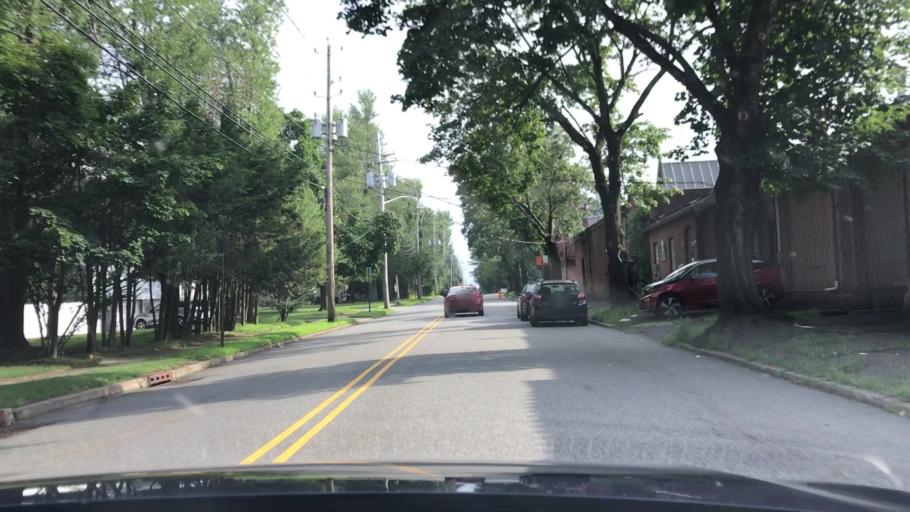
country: US
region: New Jersey
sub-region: Bergen County
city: Closter
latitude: 40.9806
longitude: -73.9583
